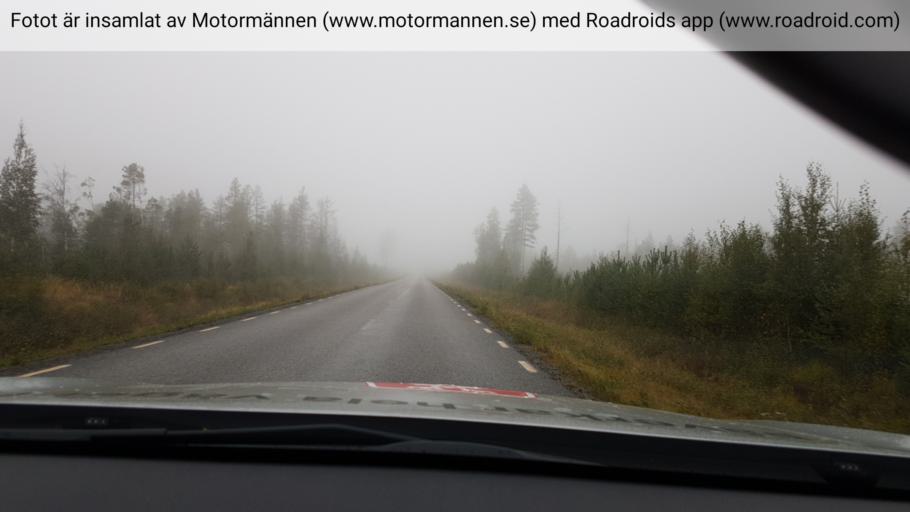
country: SE
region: Vaesterbotten
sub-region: Umea Kommun
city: Ersmark
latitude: 64.1842
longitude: 20.3363
